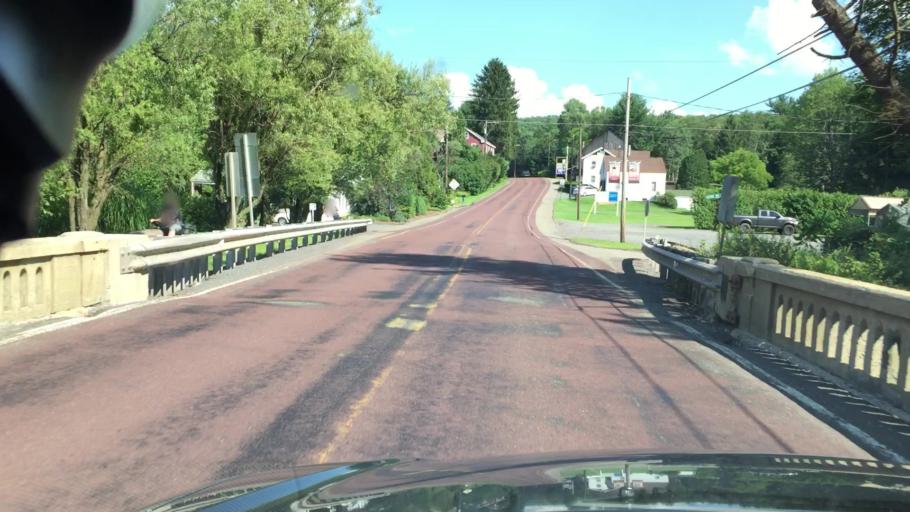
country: US
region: Pennsylvania
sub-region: Carbon County
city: Weatherly
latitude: 40.9166
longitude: -75.8550
